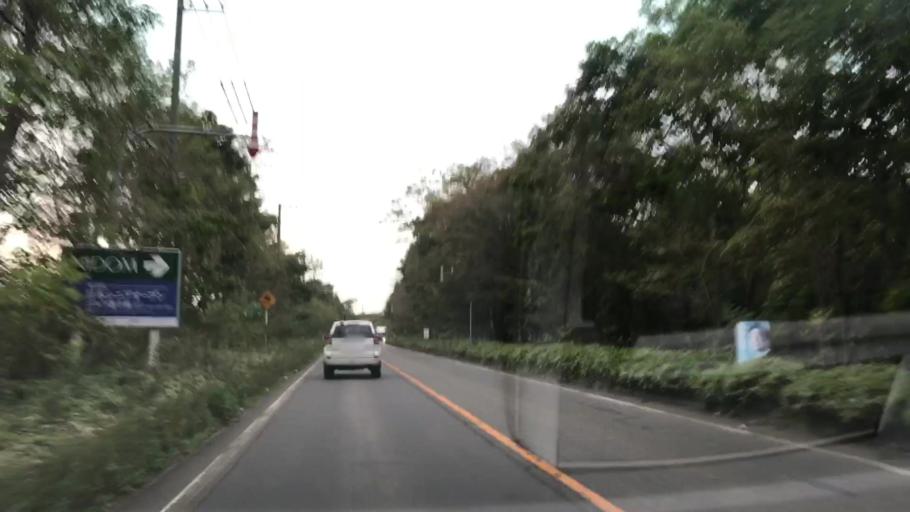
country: JP
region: Hokkaido
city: Tomakomai
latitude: 42.7056
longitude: 141.6647
